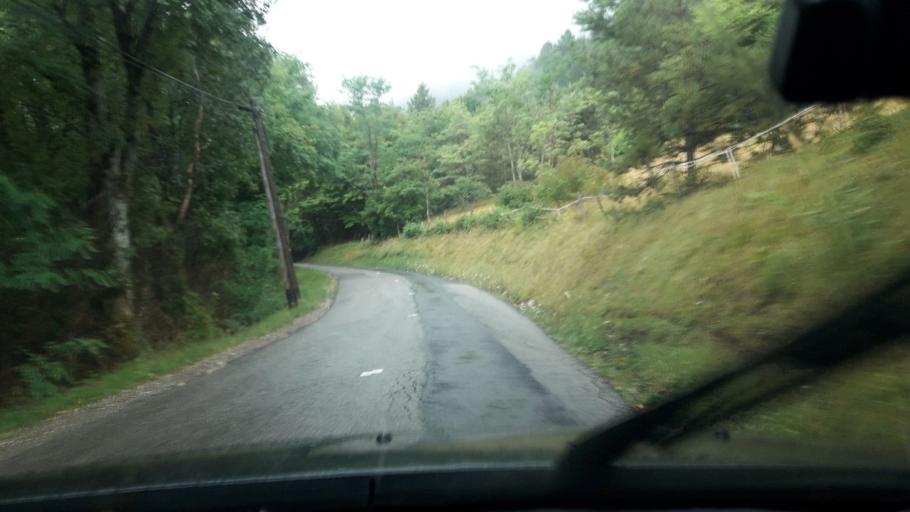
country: FR
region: Rhone-Alpes
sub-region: Departement de la Savoie
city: Saint-Baldoph
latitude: 45.5246
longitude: 5.9369
